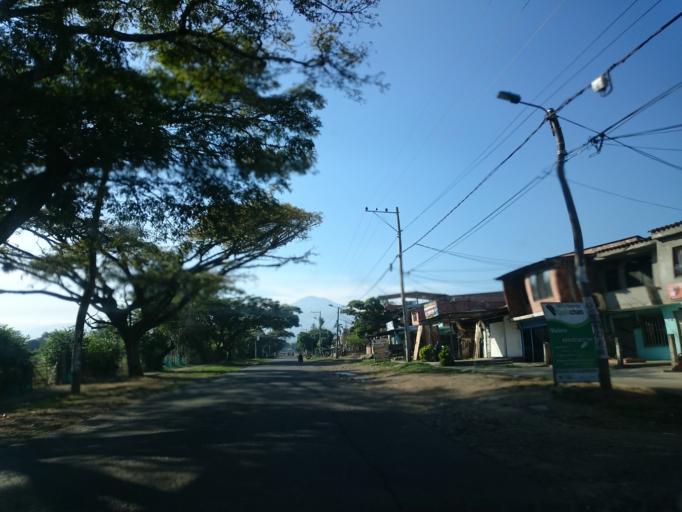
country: CO
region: Cauca
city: Santander de Quilichao
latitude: 3.0148
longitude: -76.4908
